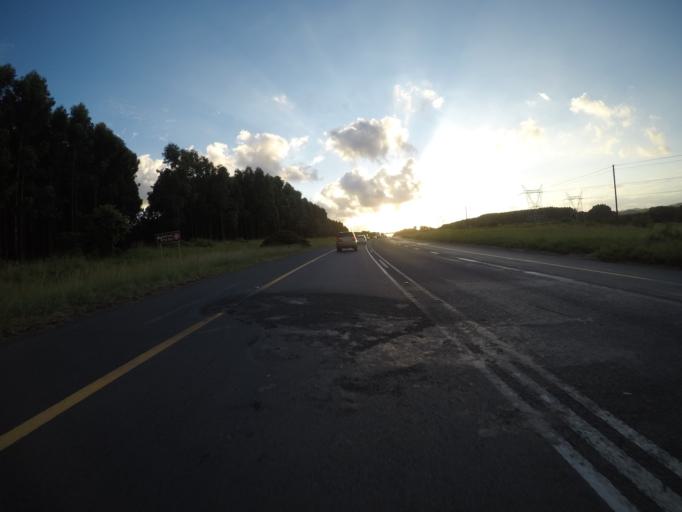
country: ZA
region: KwaZulu-Natal
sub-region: uThungulu District Municipality
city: Richards Bay
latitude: -28.6928
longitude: 32.0346
